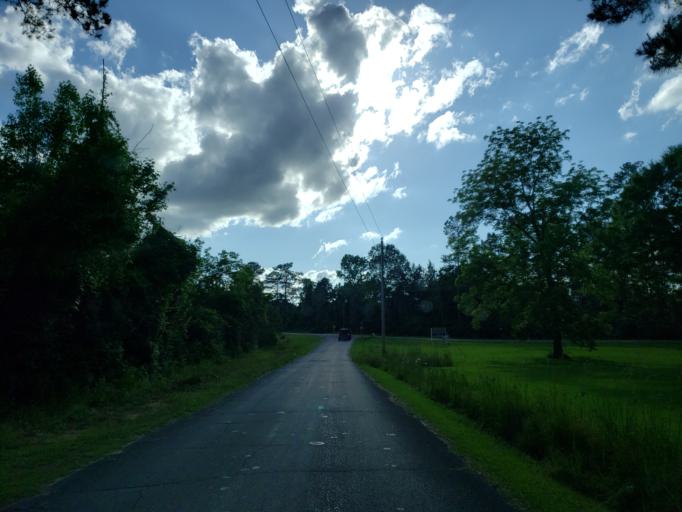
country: US
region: Mississippi
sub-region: Forrest County
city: Petal
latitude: 31.3176
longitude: -89.2054
